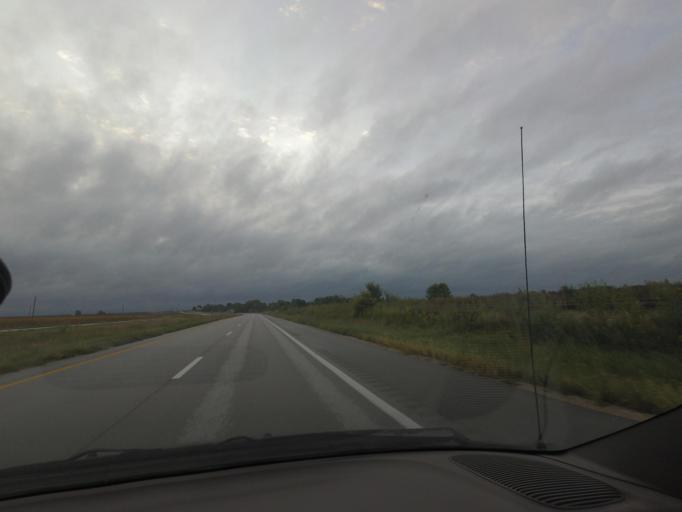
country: US
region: Missouri
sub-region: Shelby County
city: Shelbina
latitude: 39.6754
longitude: -91.9621
